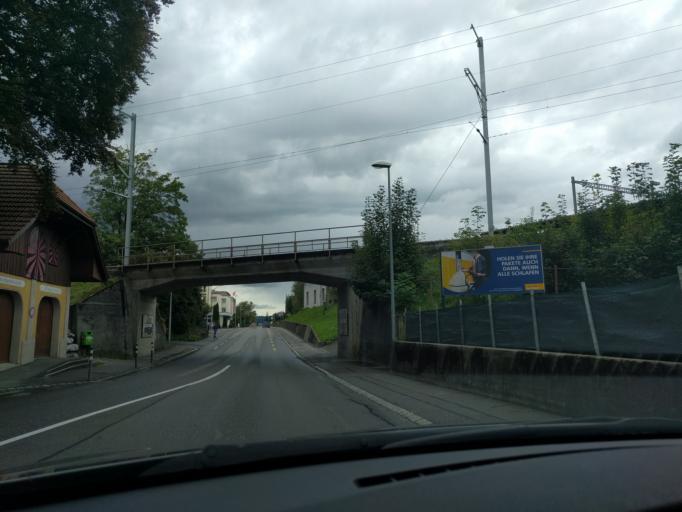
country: CH
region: Bern
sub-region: Bern-Mittelland District
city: Konolfingen
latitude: 46.8791
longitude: 7.6195
